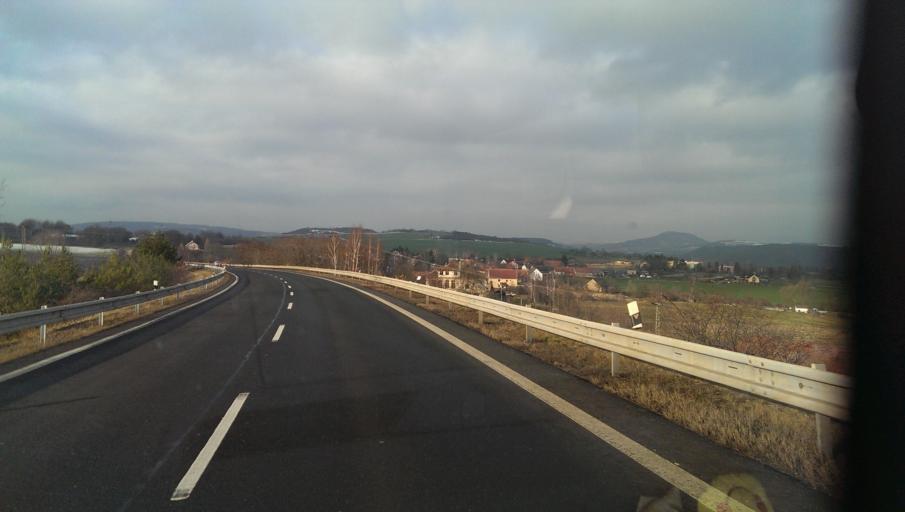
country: CZ
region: Ustecky
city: Rehlovice
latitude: 50.5872
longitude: 13.9129
